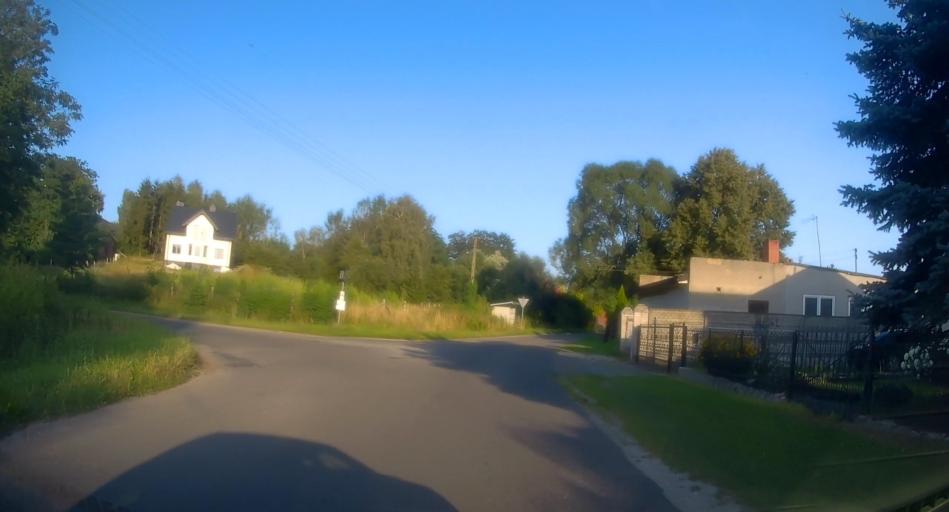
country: PL
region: Lodz Voivodeship
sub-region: Powiat skierniewicki
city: Kaweczyn Nowy
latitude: 51.8993
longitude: 20.3035
